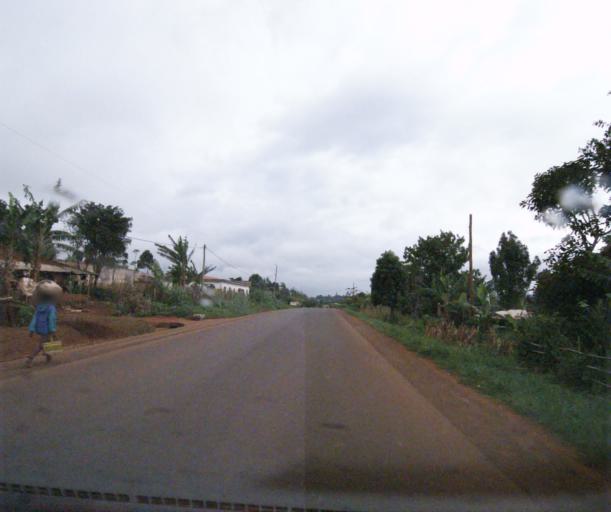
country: CM
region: West
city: Dschang
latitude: 5.4960
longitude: 10.1589
